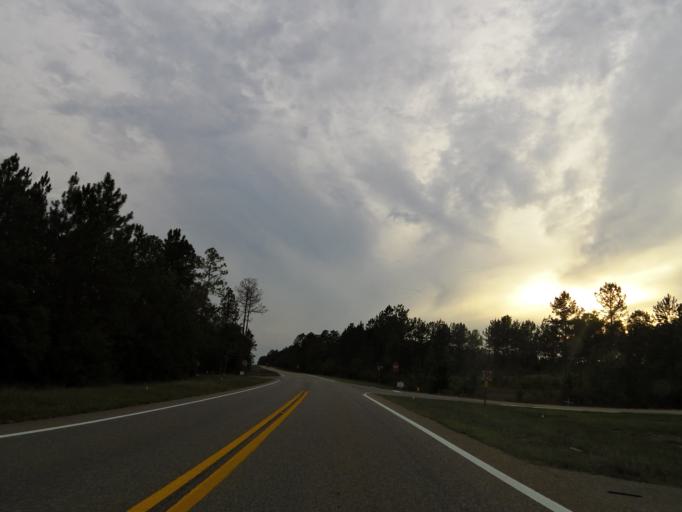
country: US
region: Alabama
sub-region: Baldwin County
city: Bay Minette
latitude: 30.9502
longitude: -87.6674
